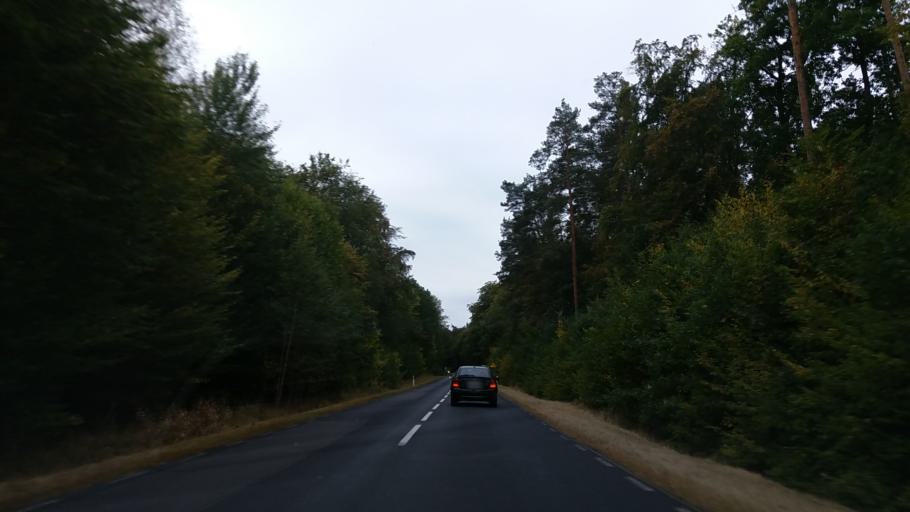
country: PL
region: Lubusz
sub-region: Powiat gorzowski
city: Klodawa
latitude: 52.8457
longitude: 15.1999
